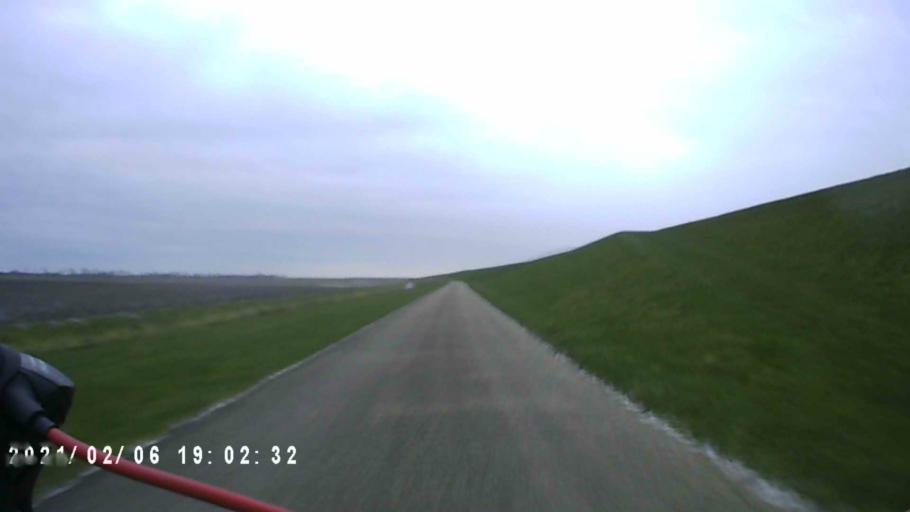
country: NL
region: Groningen
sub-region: Gemeente Winsum
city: Winsum
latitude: 53.4235
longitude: 6.4832
